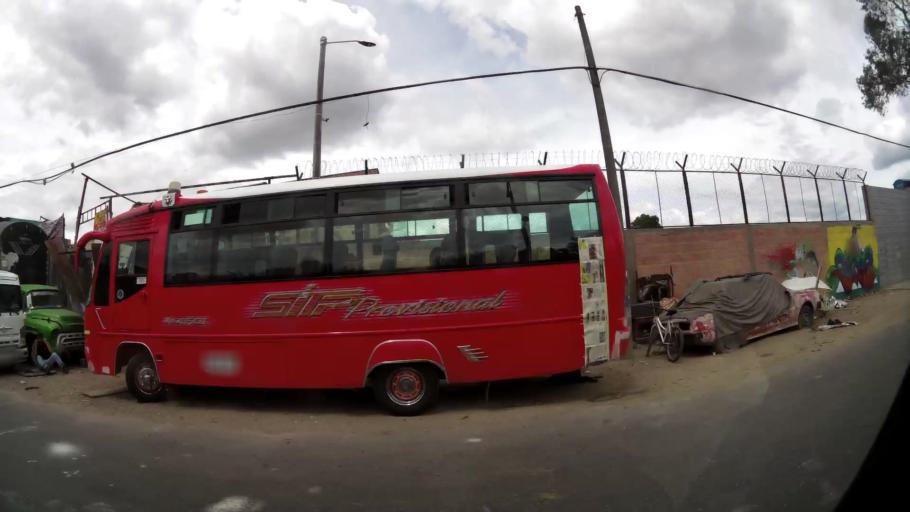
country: CO
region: Cundinamarca
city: Funza
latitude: 4.7079
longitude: -74.1411
